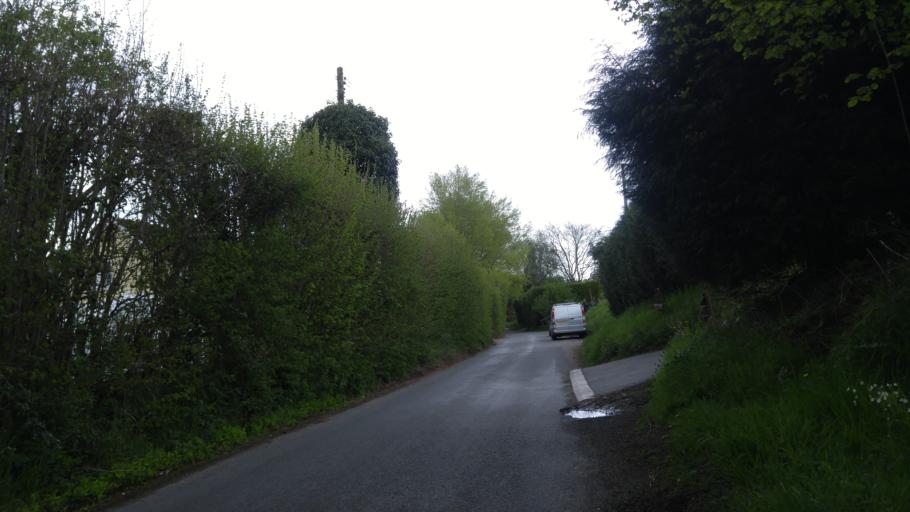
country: GB
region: England
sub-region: Suffolk
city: Sudbury
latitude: 51.9858
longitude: 0.7446
